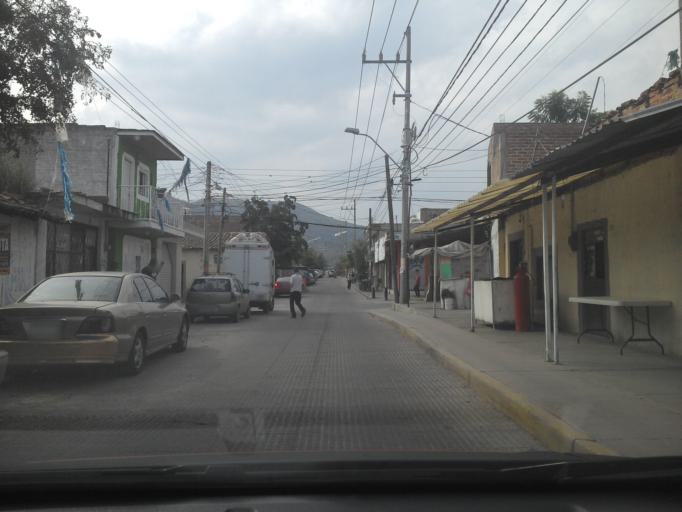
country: MX
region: Jalisco
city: Tlajomulco de Zuniga
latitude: 20.4774
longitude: -103.4459
